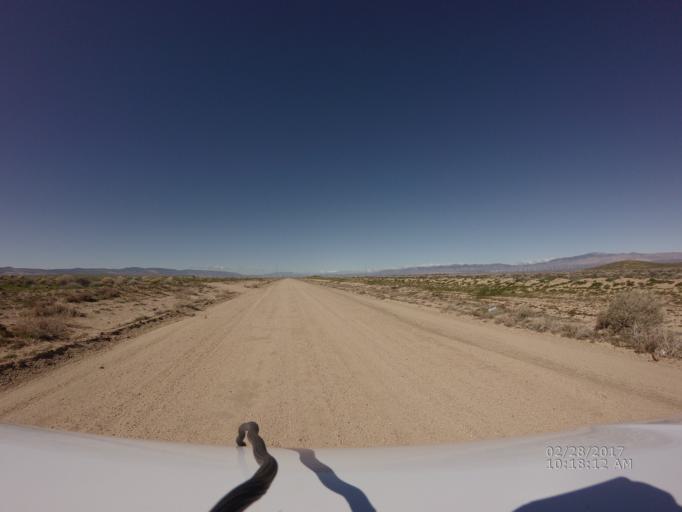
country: US
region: California
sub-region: Kern County
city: Rosamond
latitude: 34.7910
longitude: -118.3031
